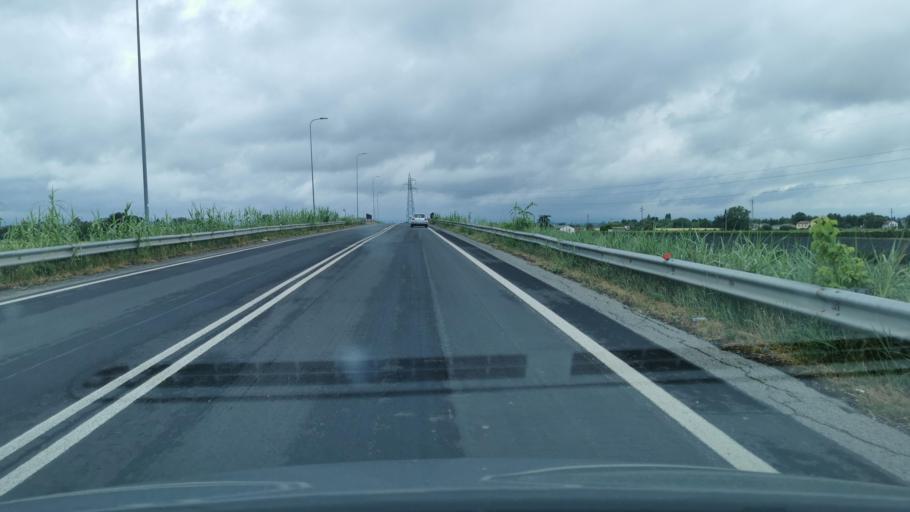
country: IT
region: Emilia-Romagna
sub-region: Provincia di Ravenna
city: Granarolo
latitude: 44.3697
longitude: 11.9411
